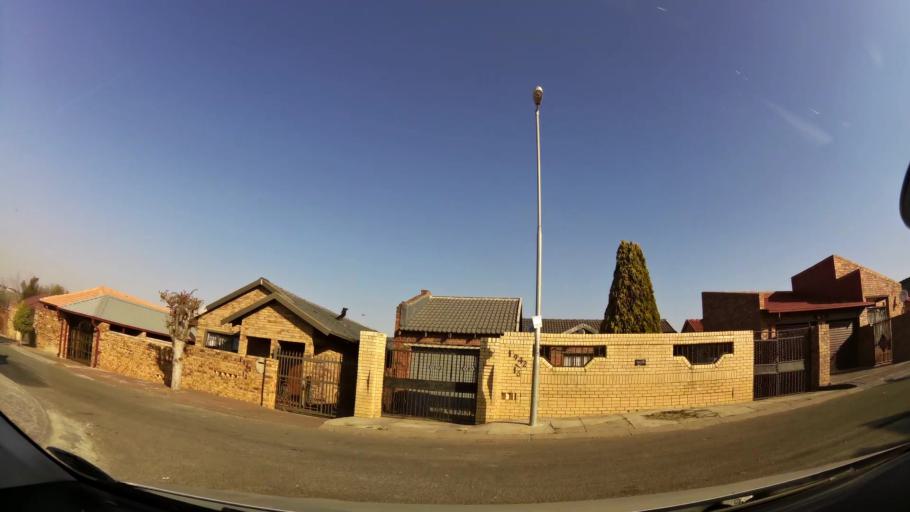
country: ZA
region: Gauteng
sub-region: City of Johannesburg Metropolitan Municipality
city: Soweto
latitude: -26.2674
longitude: 27.8795
